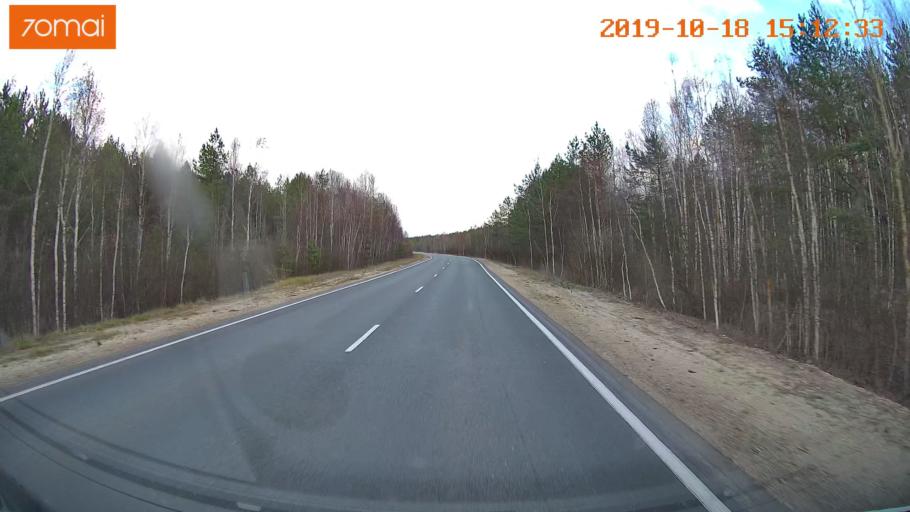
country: RU
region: Vladimir
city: Gus'-Khrustal'nyy
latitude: 55.5769
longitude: 40.7008
